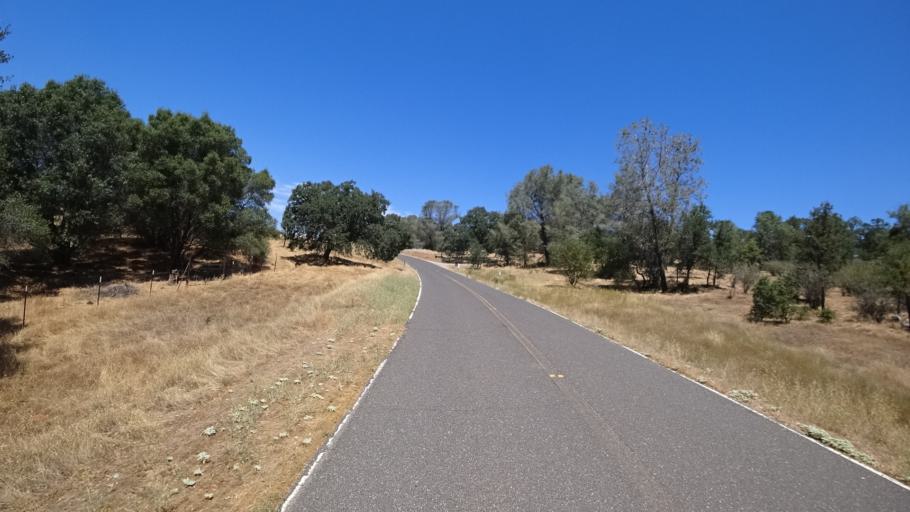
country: US
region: California
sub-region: Calaveras County
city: Angels Camp
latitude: 38.0724
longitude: -120.5699
